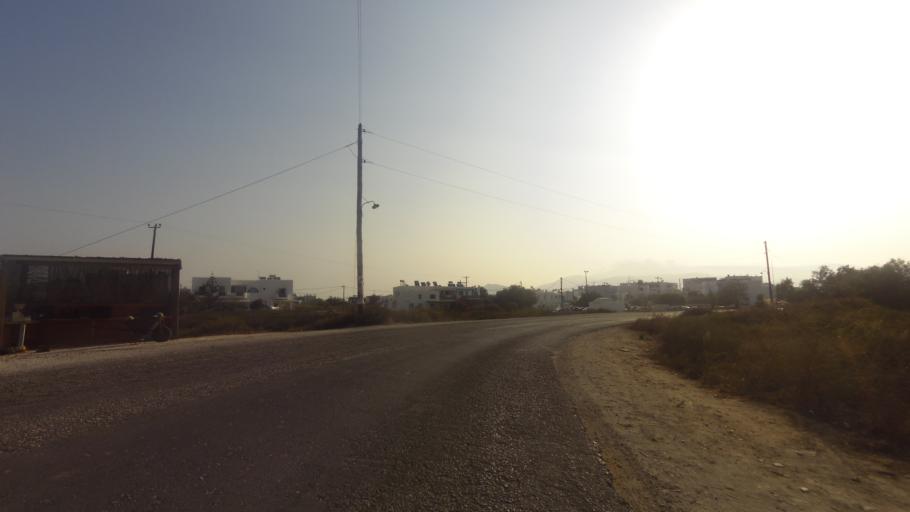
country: GR
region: South Aegean
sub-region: Nomos Kykladon
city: Antiparos
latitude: 37.0378
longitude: 25.0813
